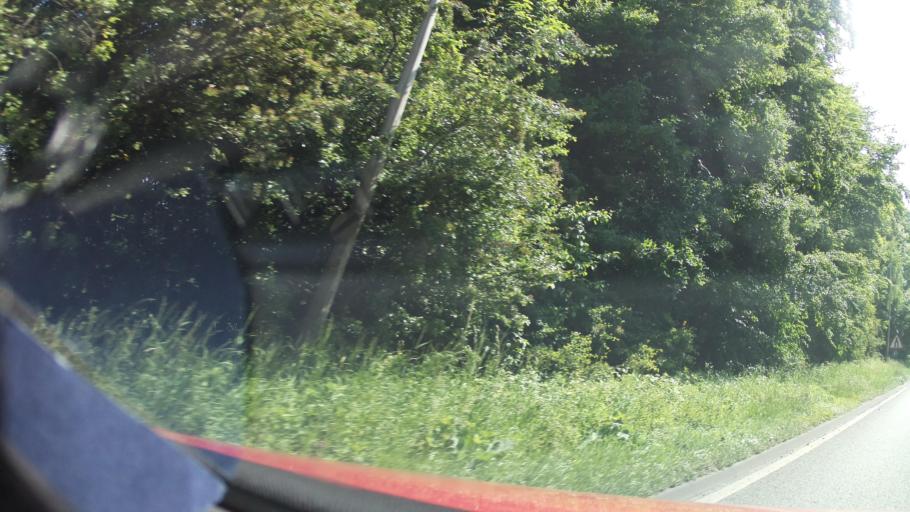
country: GB
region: England
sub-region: North Lincolnshire
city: Broughton
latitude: 53.5530
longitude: -0.5764
